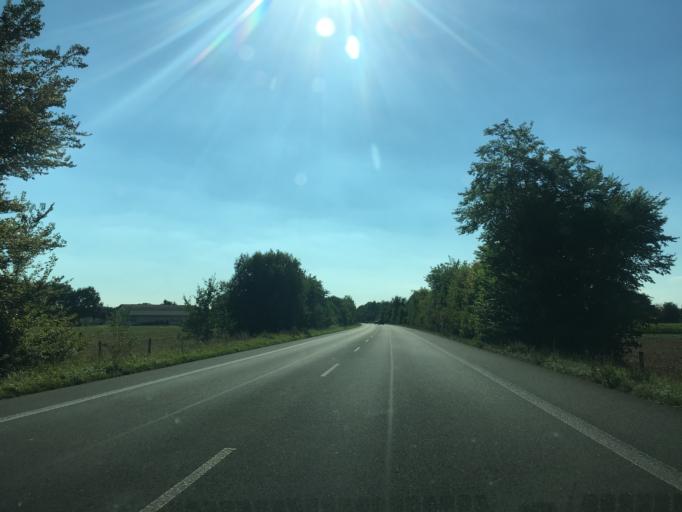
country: DE
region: North Rhine-Westphalia
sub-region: Regierungsbezirk Detmold
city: Rheda-Wiedenbruck
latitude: 51.8755
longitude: 8.2730
